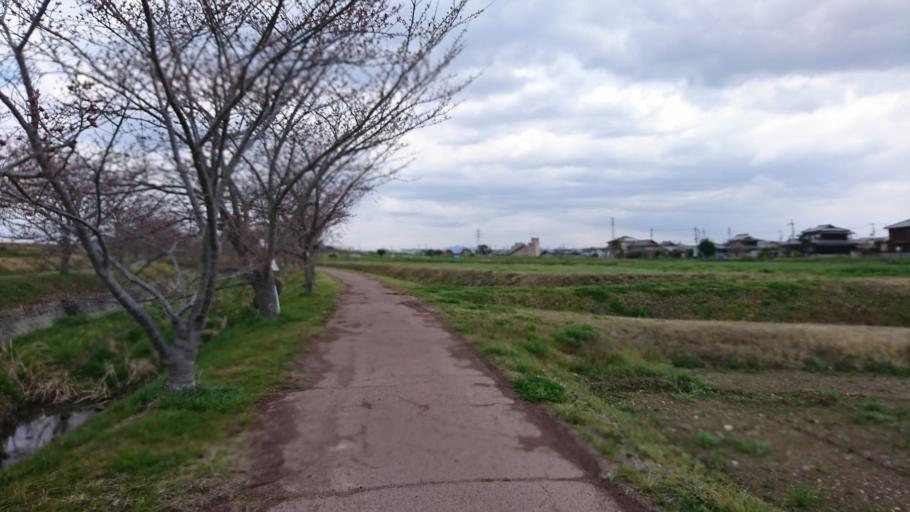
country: JP
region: Hyogo
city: Kakogawacho-honmachi
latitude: 34.7546
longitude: 134.9078
